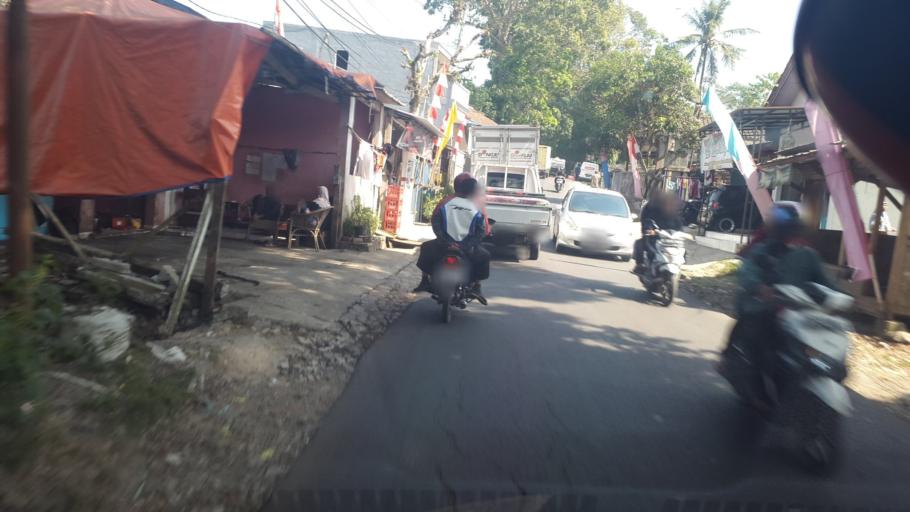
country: ID
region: West Java
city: Cicurug
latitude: -6.8502
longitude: 106.7536
